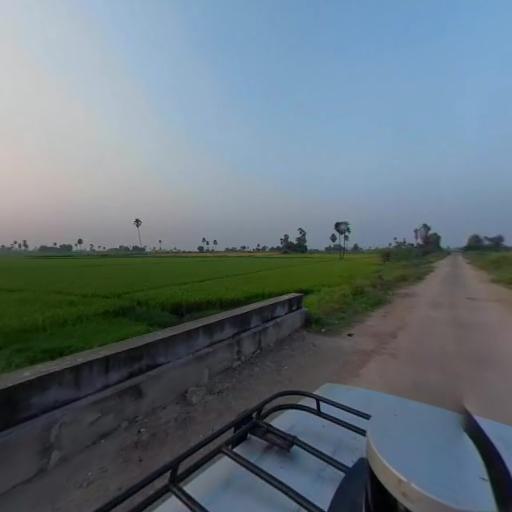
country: IN
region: Telangana
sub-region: Nalgonda
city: Suriapet
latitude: 17.0610
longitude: 79.5473
